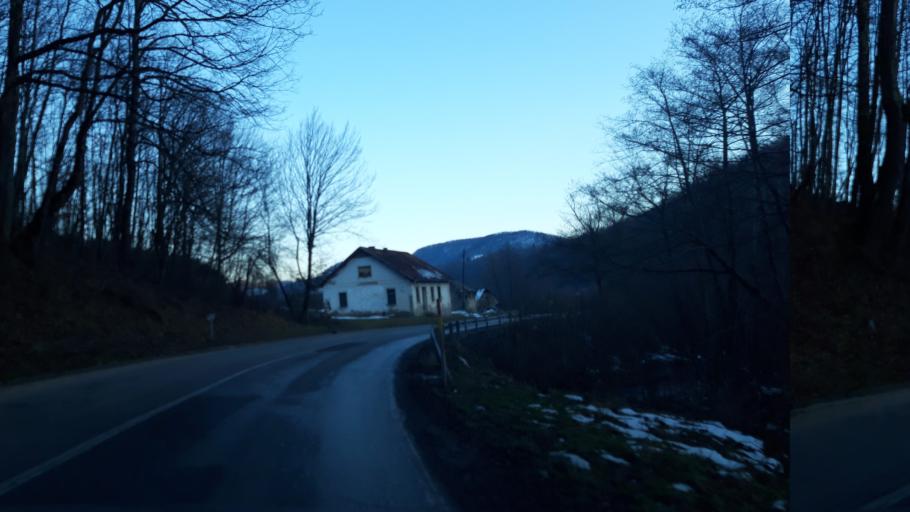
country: BA
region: Republika Srpska
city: Milici
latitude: 44.1684
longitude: 19.0323
